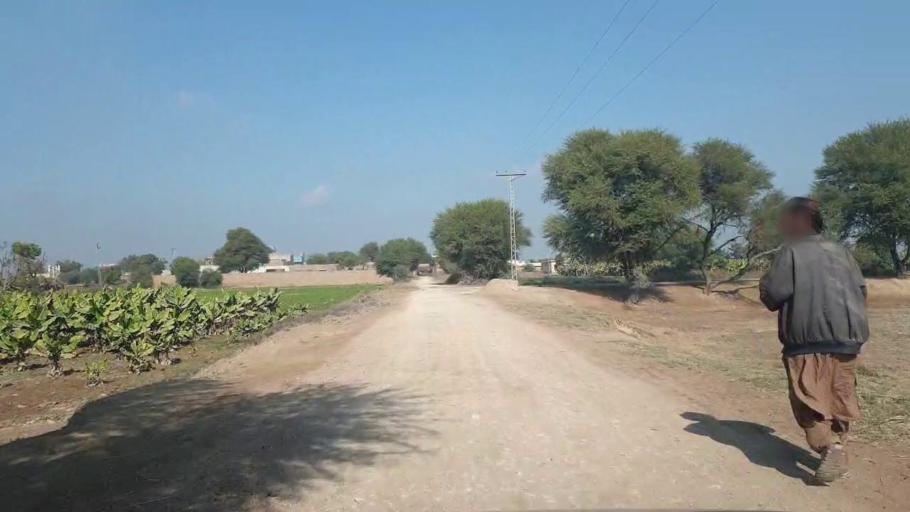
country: PK
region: Sindh
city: Shahdadpur
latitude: 25.9301
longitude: 68.5859
